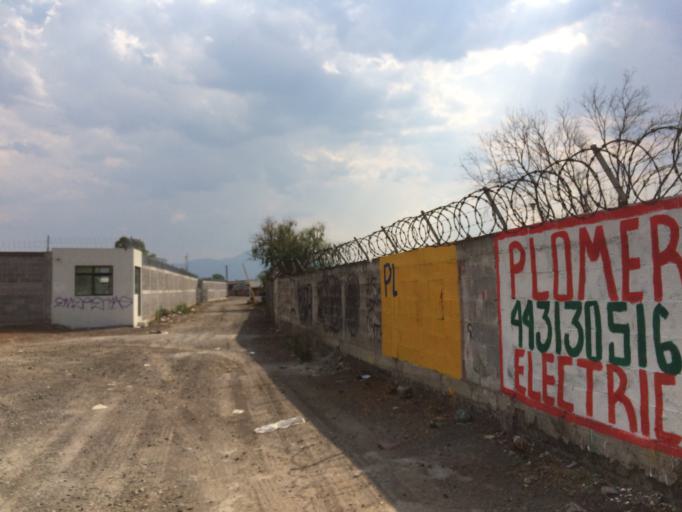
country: MX
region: Michoacan
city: Morelia
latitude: 19.6968
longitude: -101.2185
